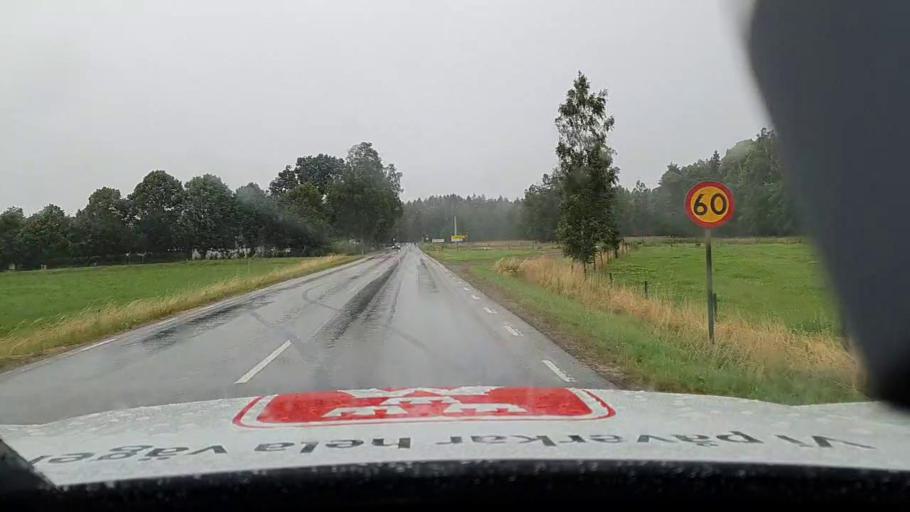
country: SE
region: Vaestra Goetaland
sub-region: Toreboda Kommun
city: Toereboda
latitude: 58.6796
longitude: 14.1324
